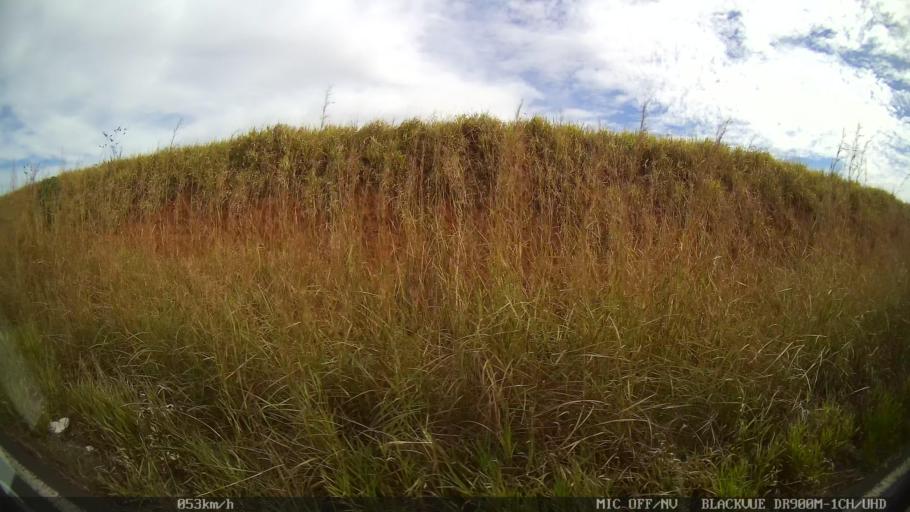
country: BR
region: Sao Paulo
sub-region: Catanduva
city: Catanduva
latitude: -21.1742
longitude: -48.9624
